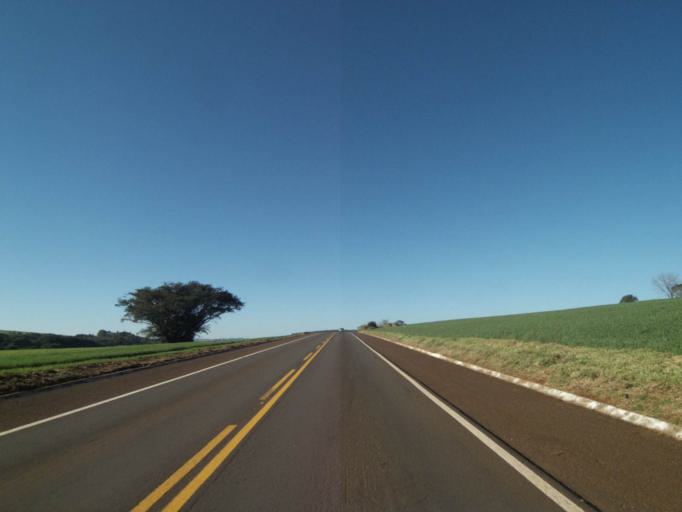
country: BR
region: Parana
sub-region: Londrina
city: Londrina
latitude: -23.5530
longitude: -51.1203
